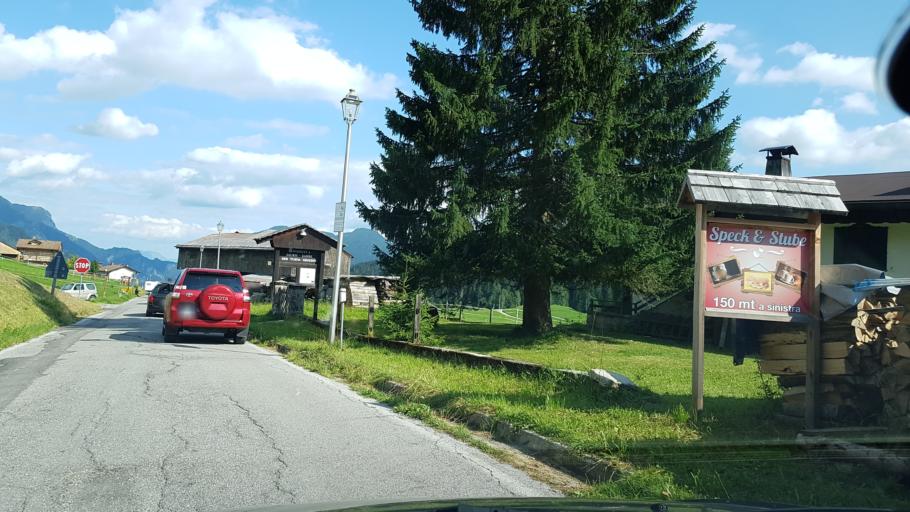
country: IT
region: Friuli Venezia Giulia
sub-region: Provincia di Udine
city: Sauris di Sotto
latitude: 46.4685
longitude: 12.6787
